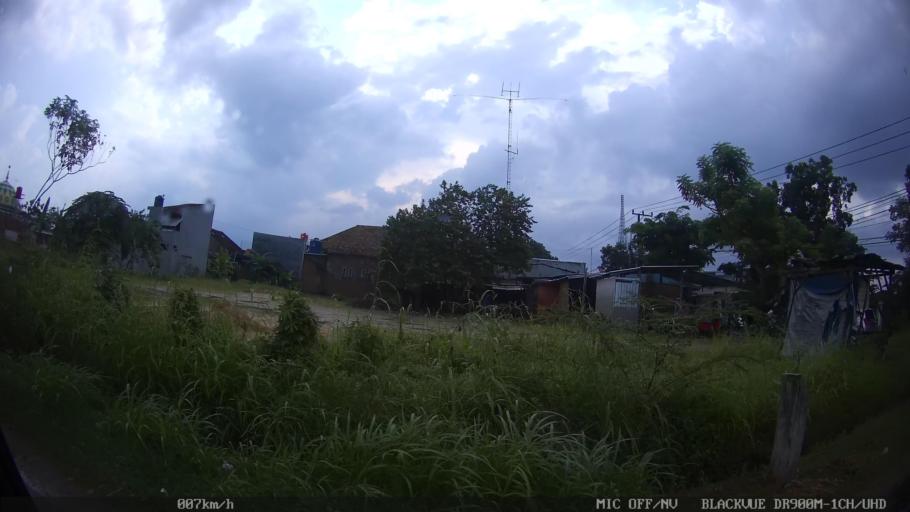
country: ID
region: Lampung
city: Kedaton
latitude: -5.3855
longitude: 105.2997
